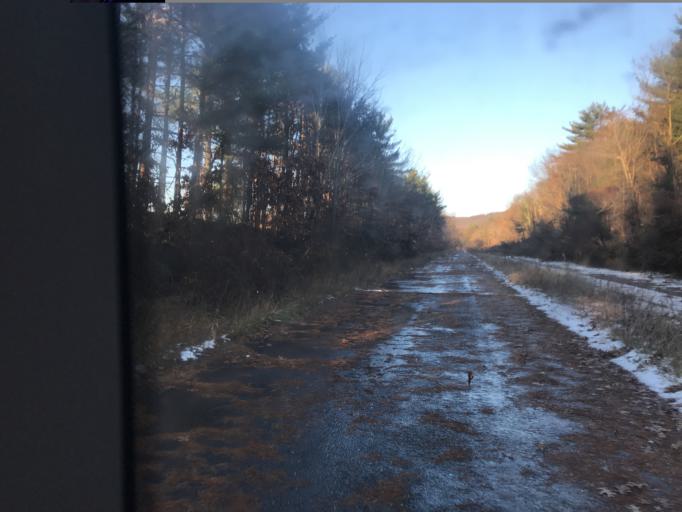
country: US
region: Pennsylvania
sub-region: Bedford County
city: Earlston
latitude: 40.0056
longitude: -78.2204
